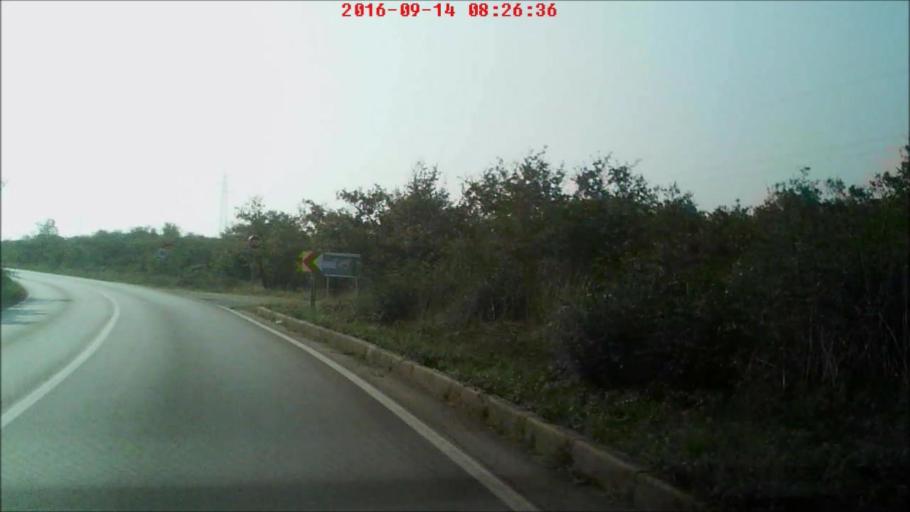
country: HR
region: Zadarska
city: Vrsi
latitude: 44.1945
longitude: 15.2562
